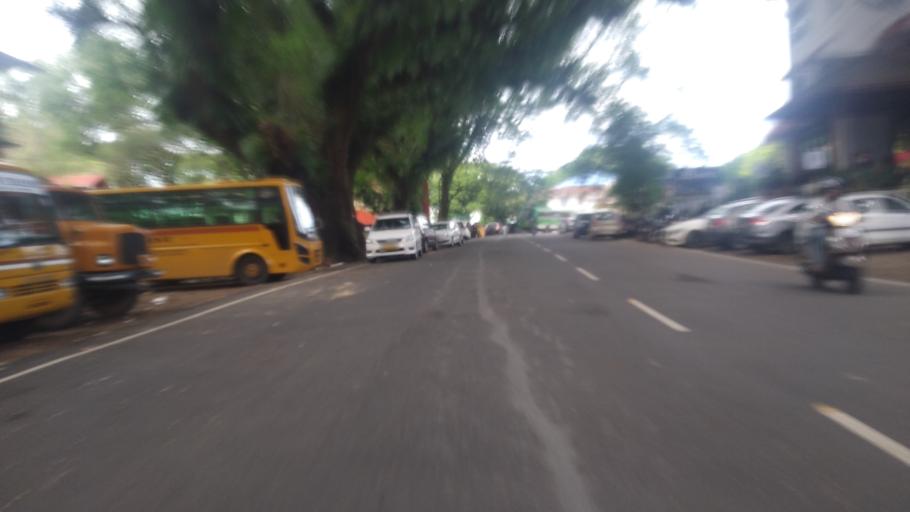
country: IN
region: Kerala
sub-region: Ernakulam
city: Cochin
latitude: 9.9672
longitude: 76.2444
